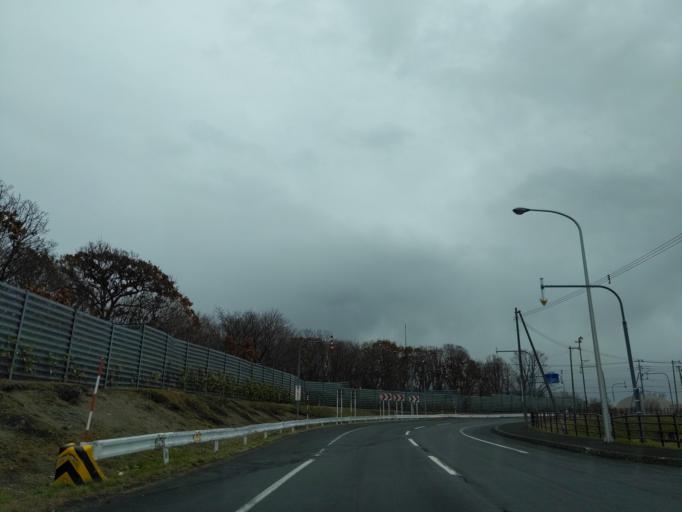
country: JP
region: Hokkaido
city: Ishikari
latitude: 43.1948
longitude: 141.2935
